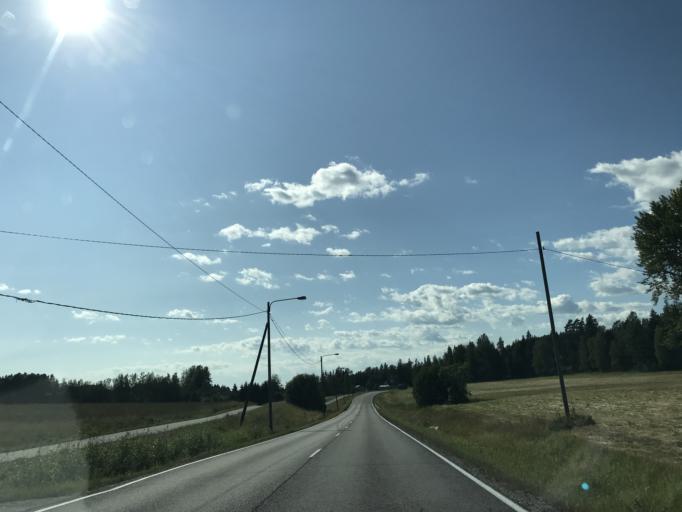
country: FI
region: Uusimaa
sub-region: Helsinki
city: Tuusula
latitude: 60.4010
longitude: 24.9212
